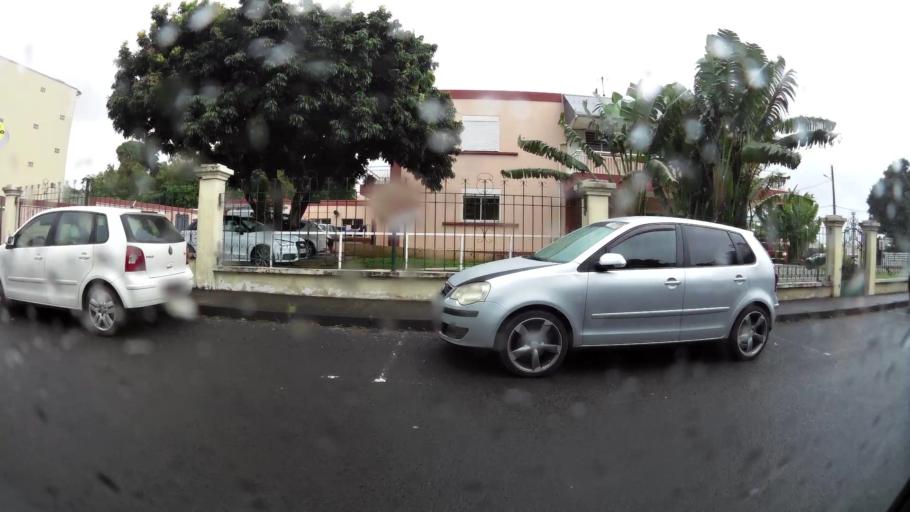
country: RE
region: Reunion
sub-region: Reunion
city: Saint-Andre
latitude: -20.9597
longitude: 55.6531
